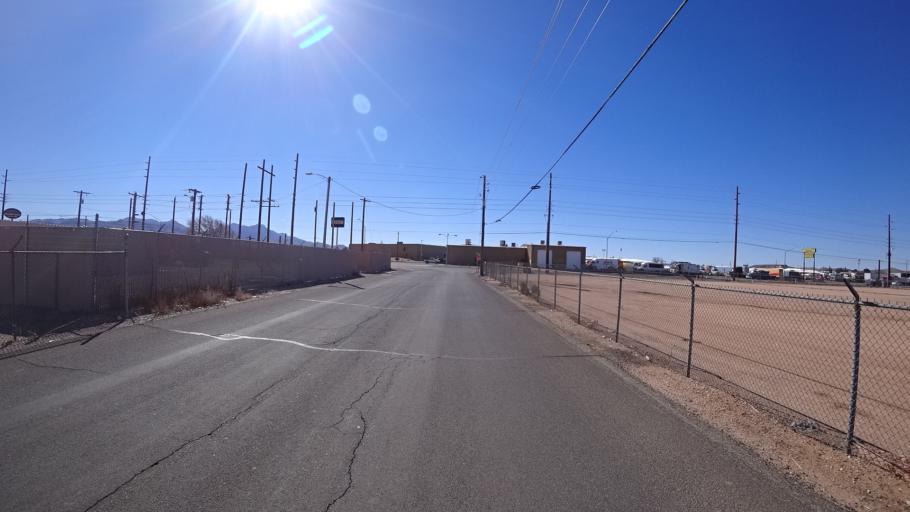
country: US
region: Arizona
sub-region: Mohave County
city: New Kingman-Butler
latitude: 35.2255
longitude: -114.0056
